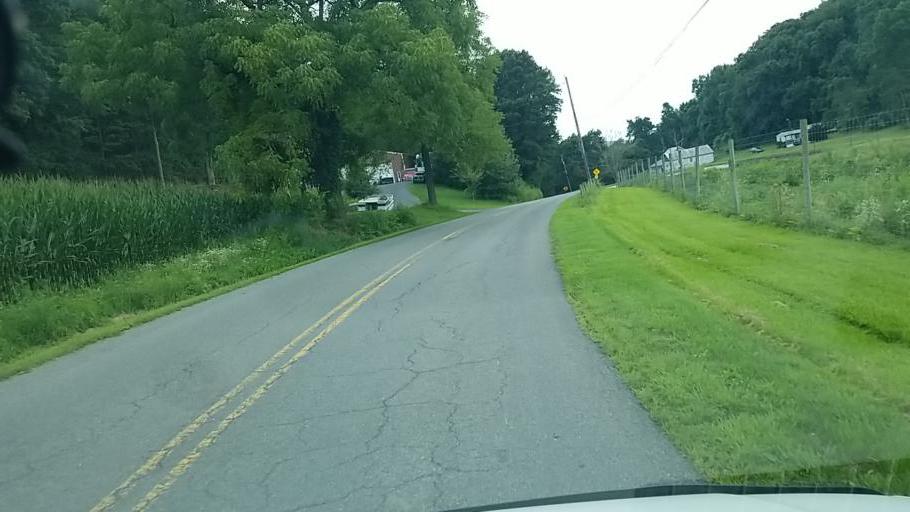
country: US
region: Pennsylvania
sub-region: Dauphin County
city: Elizabethville
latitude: 40.6531
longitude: -76.8620
